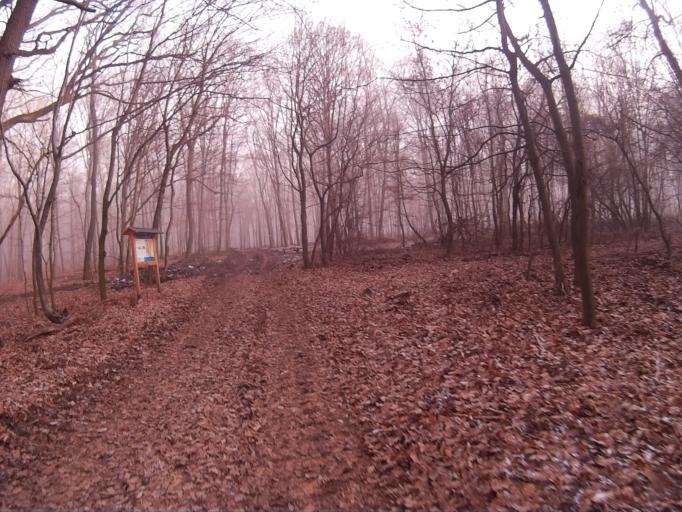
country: HU
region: Komarom-Esztergom
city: Oroszlany
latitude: 47.4580
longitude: 18.3901
